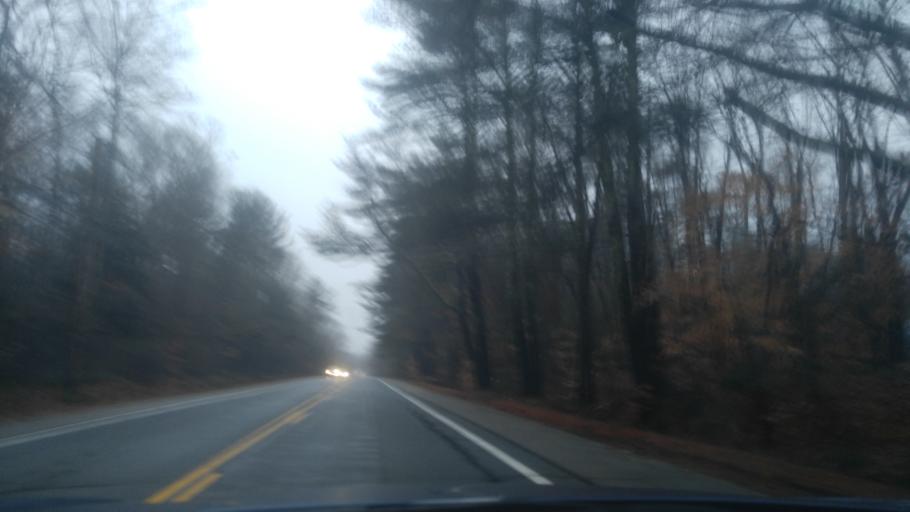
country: US
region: Rhode Island
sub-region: Washington County
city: Kingston
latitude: 41.4859
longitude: -71.5842
